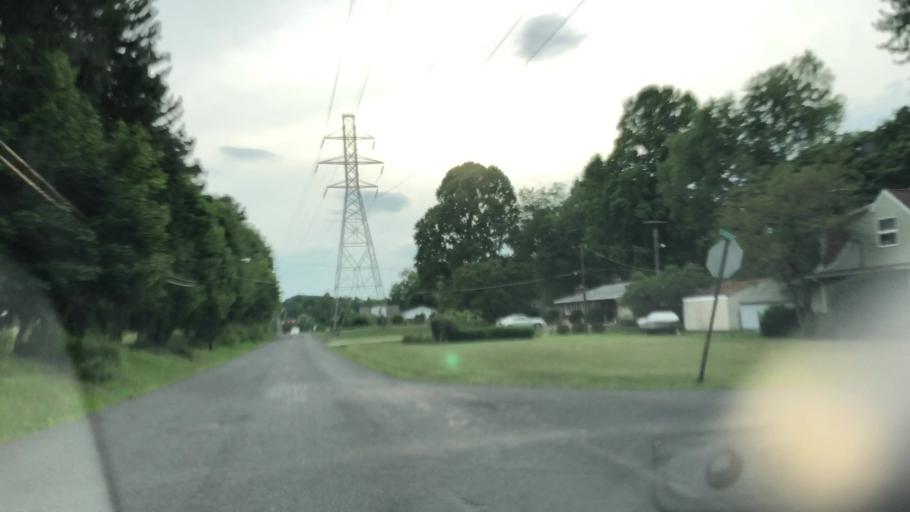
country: US
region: Ohio
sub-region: Stark County
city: North Canton
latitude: 40.8499
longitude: -81.3876
